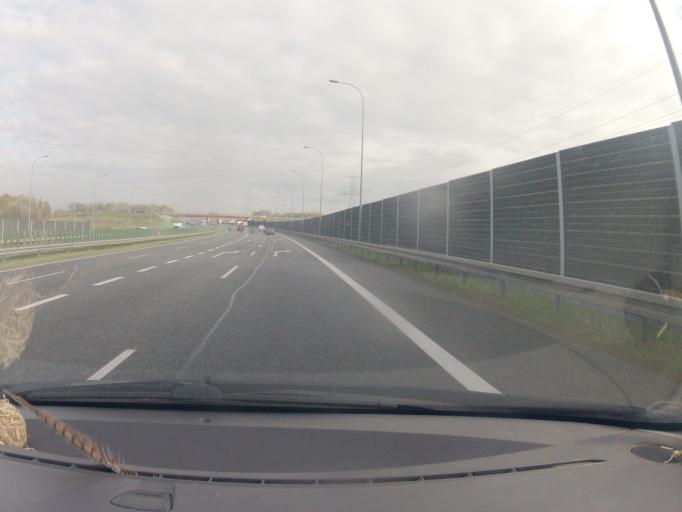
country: PL
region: Lesser Poland Voivodeship
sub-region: Powiat wielicki
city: Czarnochowice
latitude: 50.0081
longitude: 20.0566
